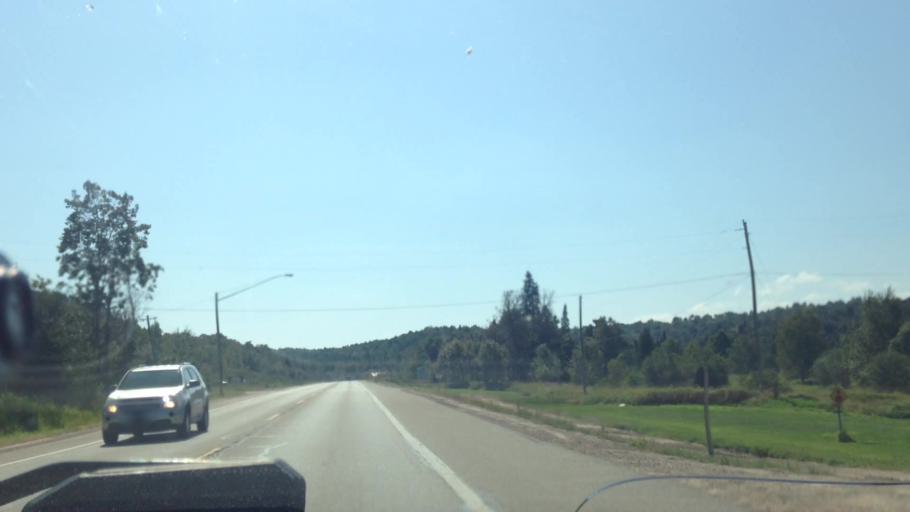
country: US
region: Michigan
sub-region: Alger County
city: Munising
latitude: 46.4001
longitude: -86.6465
